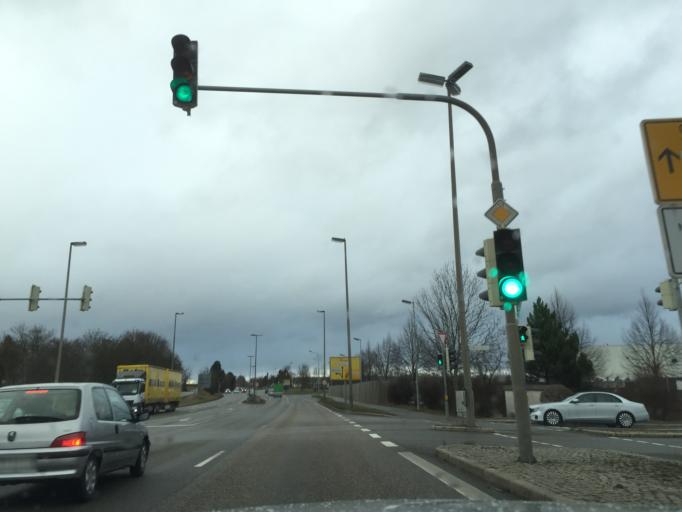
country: DE
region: Baden-Wuerttemberg
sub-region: Regierungsbezirk Stuttgart
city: Boeblingen
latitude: 48.6920
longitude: 8.9791
